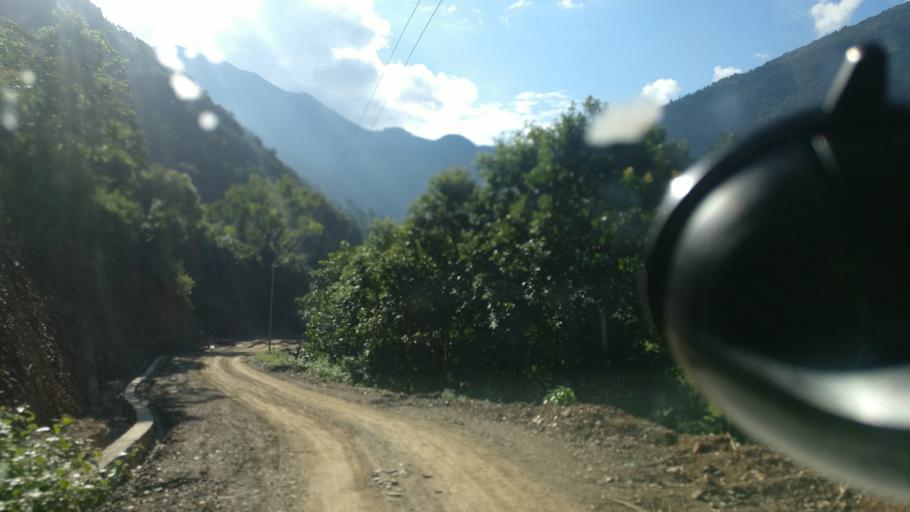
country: NP
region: Western Region
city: Baglung
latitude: 28.1472
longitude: 83.6593
